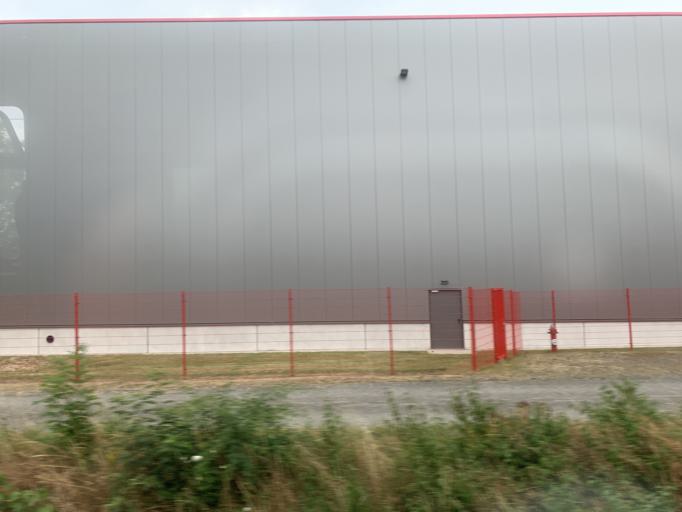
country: DE
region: North Rhine-Westphalia
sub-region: Regierungsbezirk Koln
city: Kerpen
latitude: 50.8932
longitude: 6.6550
